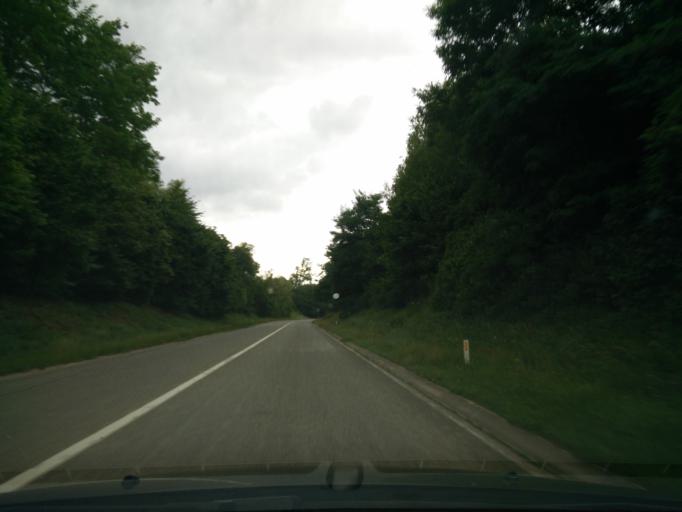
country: BE
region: Wallonia
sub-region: Province de Liege
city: Bassenge
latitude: 50.7815
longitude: 5.6375
